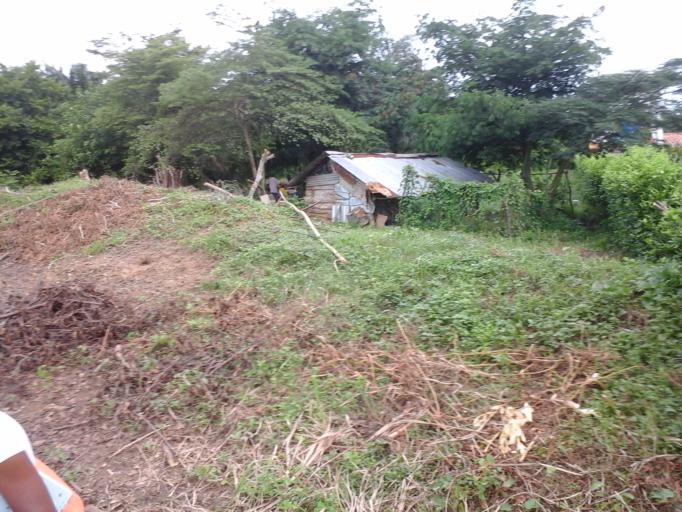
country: CO
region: Bolivar
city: Mahates
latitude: 10.1642
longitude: -75.2758
